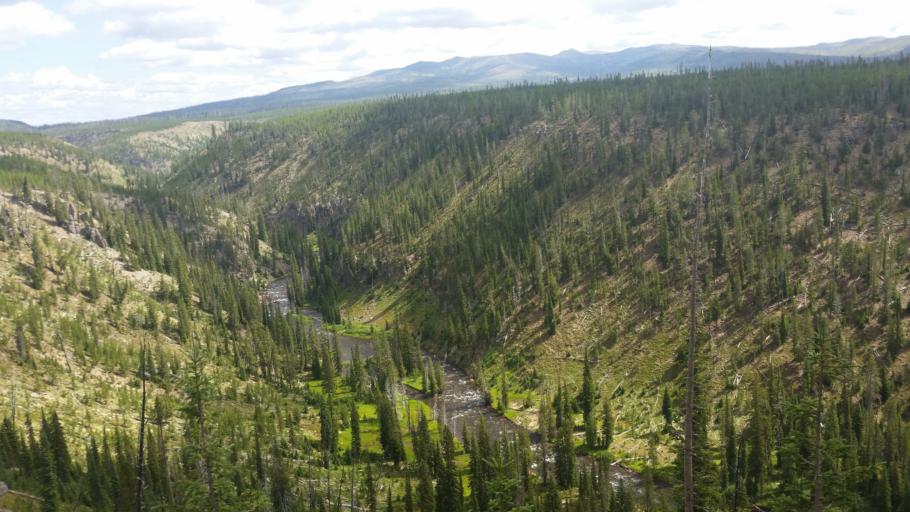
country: US
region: Montana
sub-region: Gallatin County
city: West Yellowstone
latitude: 44.2040
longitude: -110.6602
